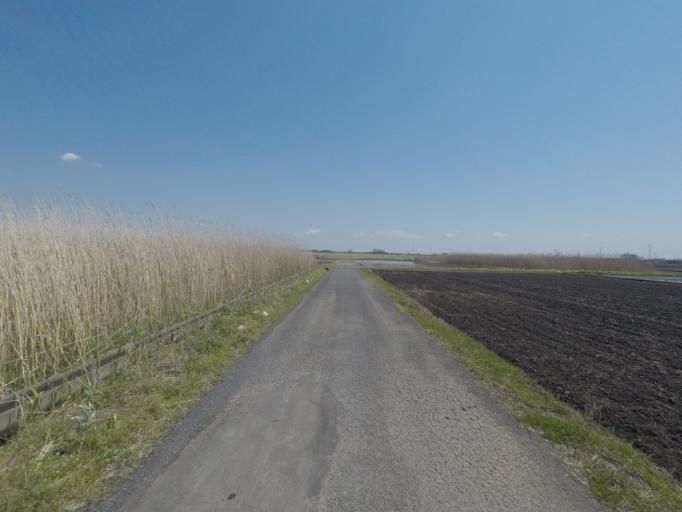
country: JP
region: Ibaraki
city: Fujishiro
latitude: 35.9443
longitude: 140.1158
